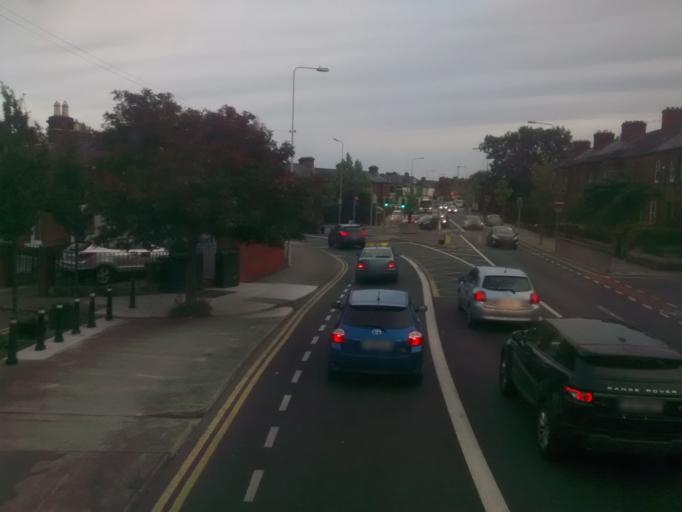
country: IE
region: Leinster
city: Glasnevin
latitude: 53.3679
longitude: -6.2731
